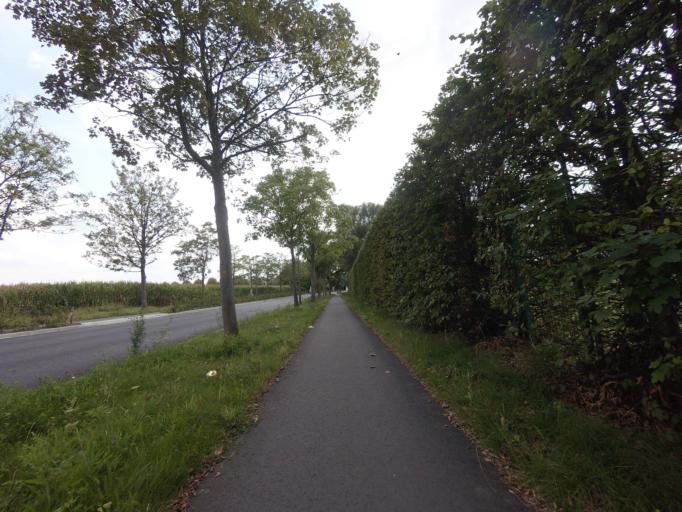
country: BE
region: Flanders
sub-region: Provincie Antwerpen
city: Aartselaar
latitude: 51.1518
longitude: 4.3942
